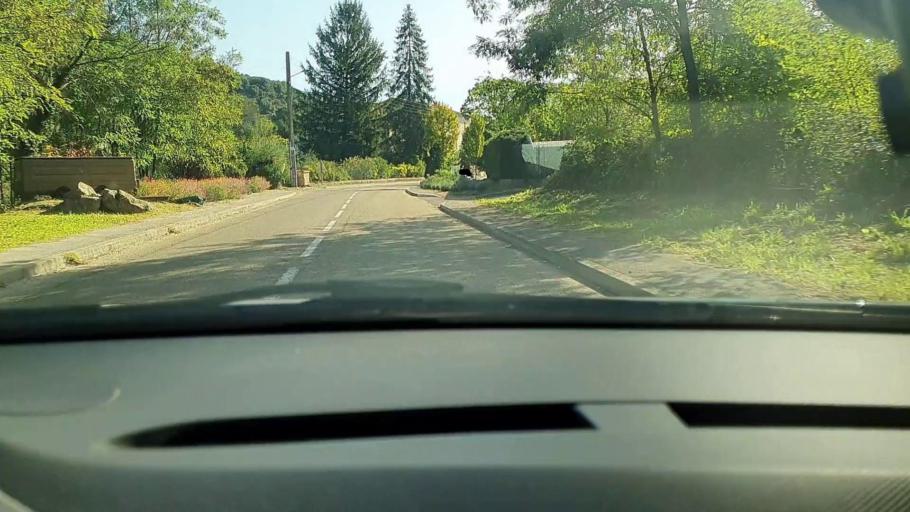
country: FR
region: Languedoc-Roussillon
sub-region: Departement du Gard
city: Saint-Florent-sur-Auzonnet
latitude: 44.2457
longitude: 4.0976
